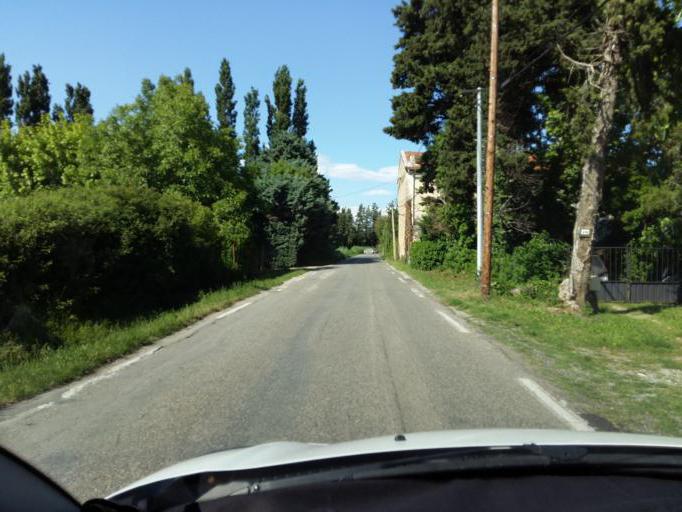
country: FR
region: Provence-Alpes-Cote d'Azur
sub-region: Departement du Vaucluse
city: Cavaillon
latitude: 43.8558
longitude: 5.0535
